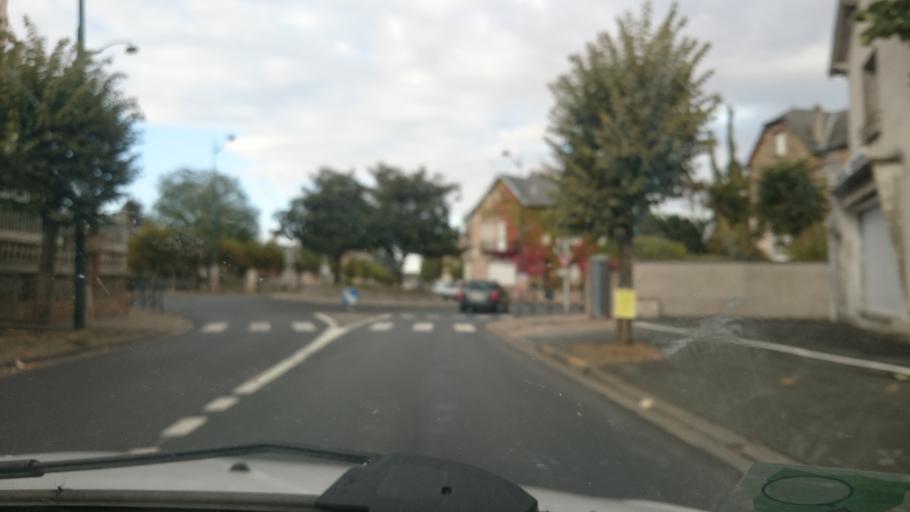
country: FR
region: Centre
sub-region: Departement de l'Indre
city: La Chatre
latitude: 46.5848
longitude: 1.9850
